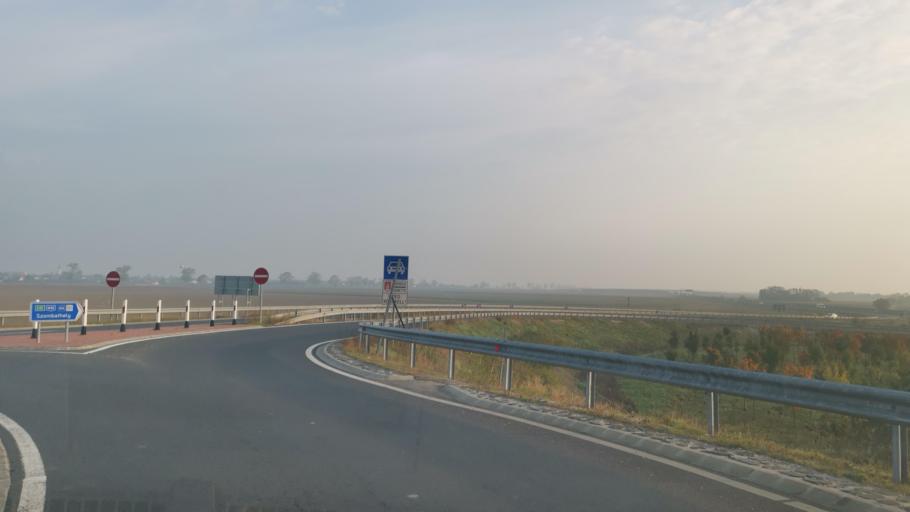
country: HU
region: Gyor-Moson-Sopron
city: Beled
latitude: 47.4521
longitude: 17.1009
